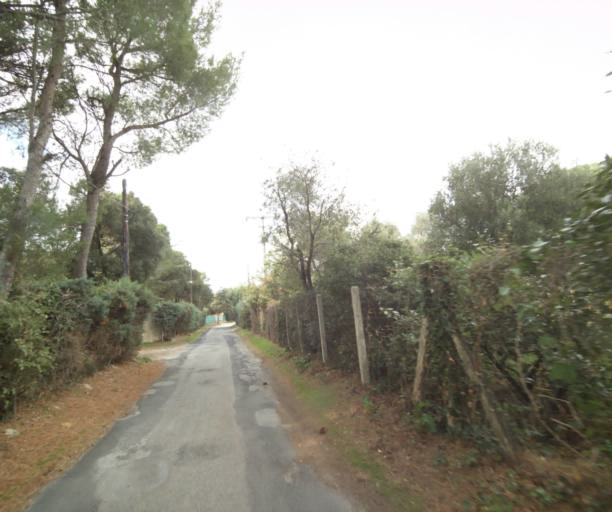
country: FR
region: Languedoc-Roussillon
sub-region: Departement des Pyrenees-Orientales
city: Argelers
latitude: 42.5439
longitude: 3.0033
